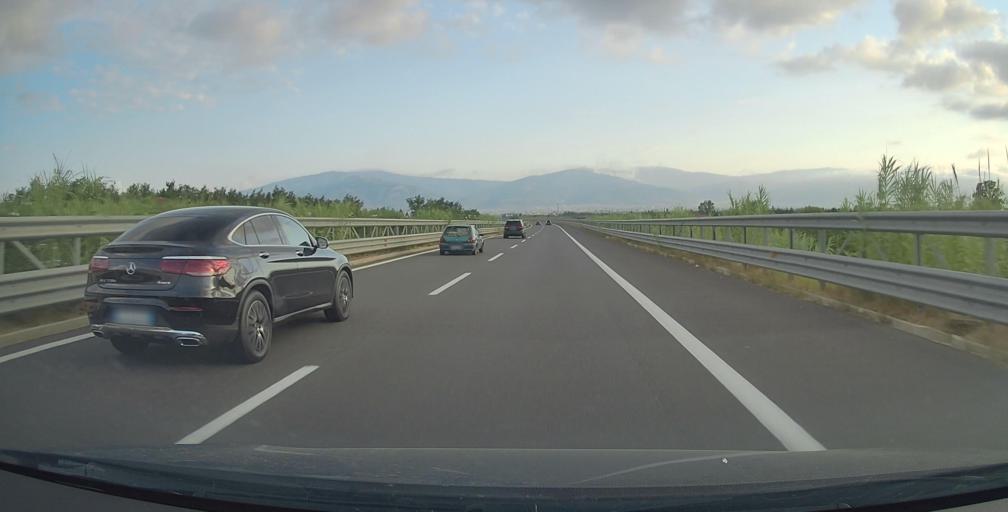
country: IT
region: Calabria
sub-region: Provincia di Catanzaro
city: Acconia
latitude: 38.8783
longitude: 16.2816
